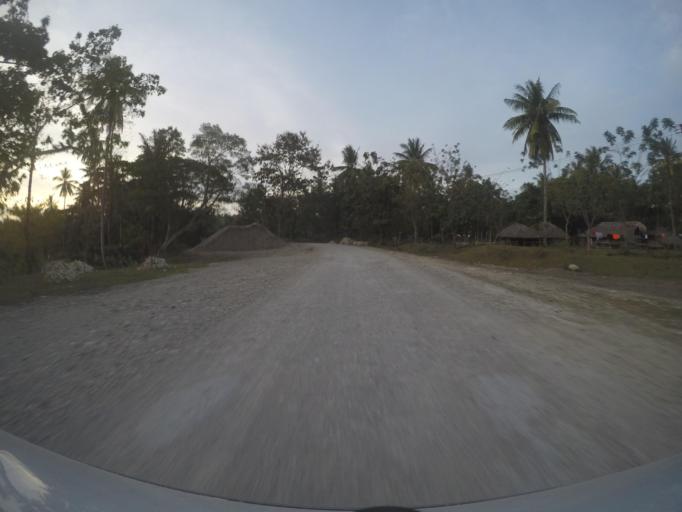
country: TL
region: Viqueque
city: Viqueque
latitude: -8.9000
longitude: 126.3929
